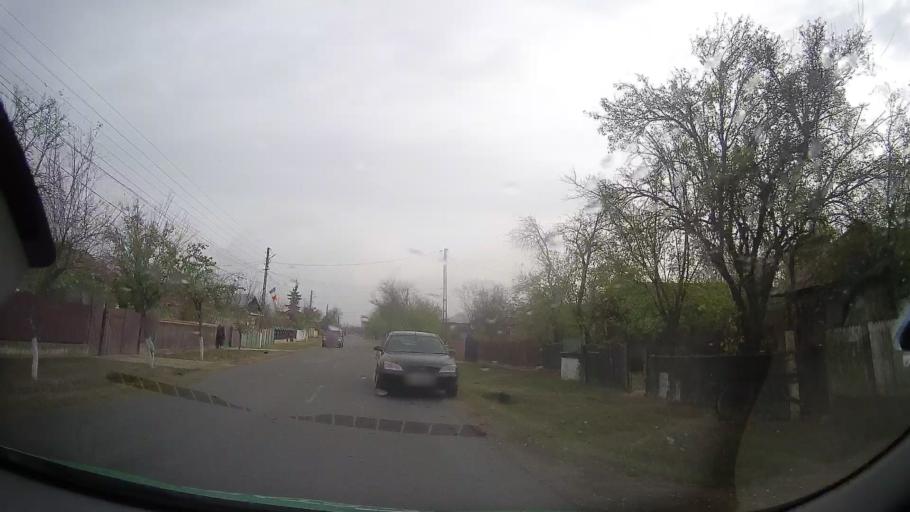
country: RO
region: Prahova
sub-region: Comuna Rafov
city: Palanca
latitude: 44.8456
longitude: 26.2312
